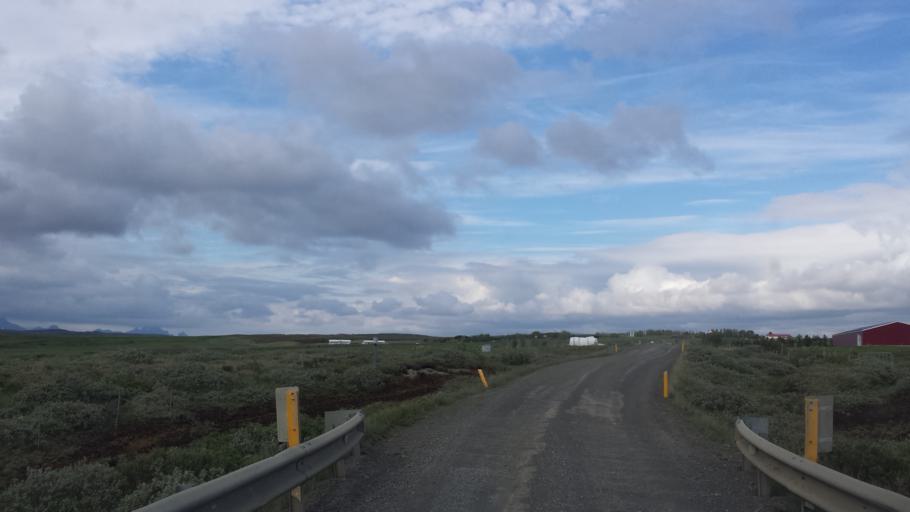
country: IS
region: South
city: Selfoss
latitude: 64.3054
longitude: -20.2415
